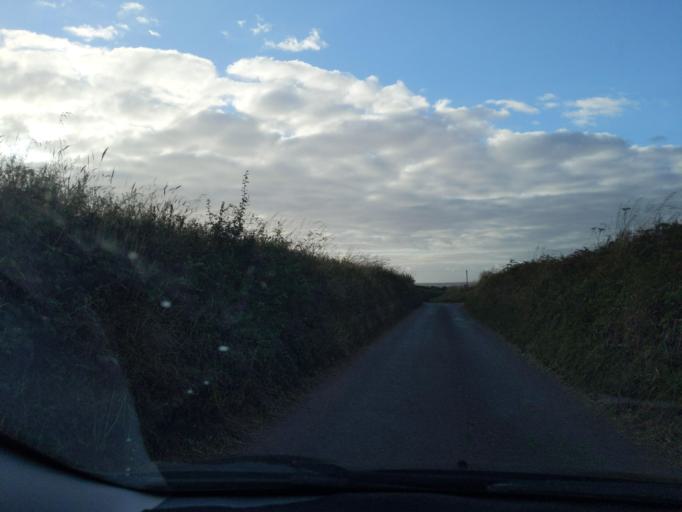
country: GB
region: England
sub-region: Devon
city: Salcombe
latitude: 50.2336
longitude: -3.8178
